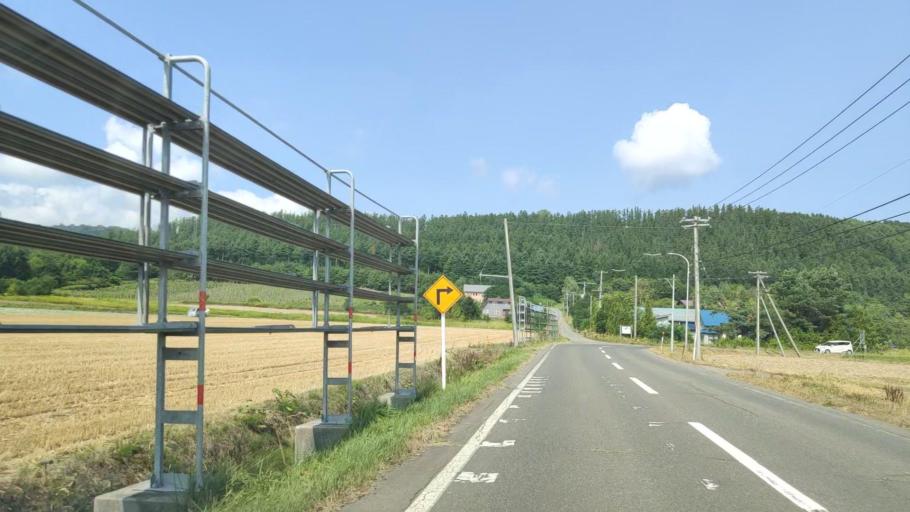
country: JP
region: Hokkaido
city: Shimo-furano
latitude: 43.3940
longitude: 142.3919
